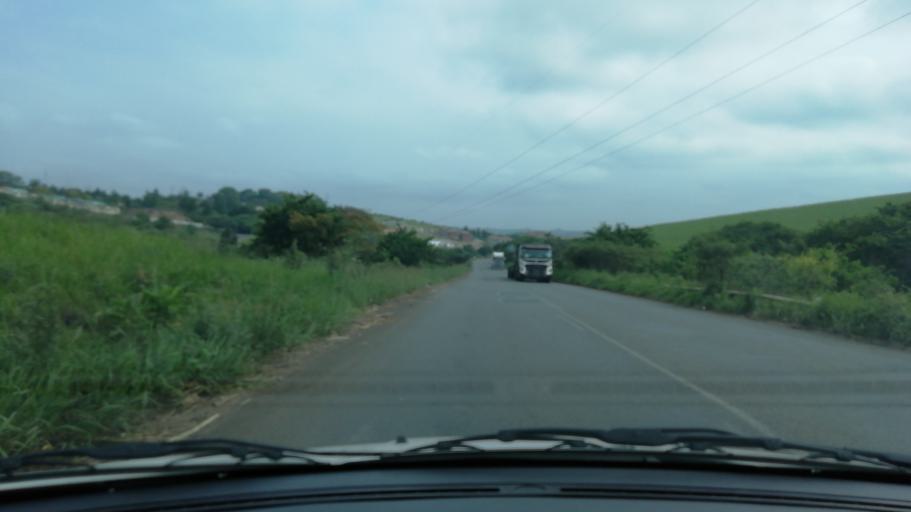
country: ZA
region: KwaZulu-Natal
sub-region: uThungulu District Municipality
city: Empangeni
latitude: -28.7448
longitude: 31.8807
